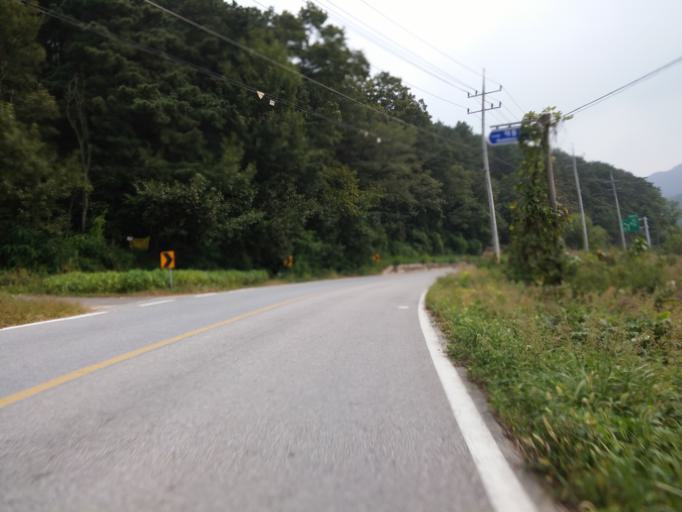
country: KR
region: Chungcheongbuk-do
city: Okcheon
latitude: 36.4235
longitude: 127.7727
